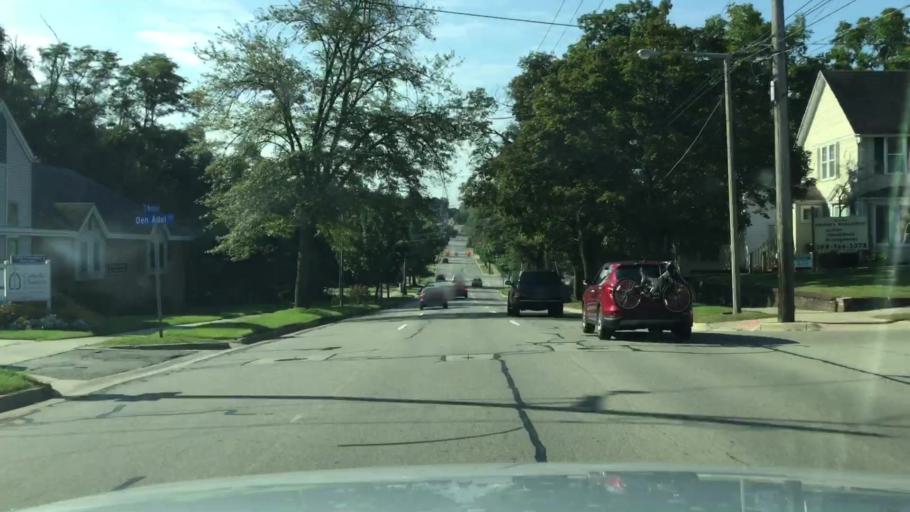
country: US
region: Michigan
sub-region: Kalamazoo County
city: Kalamazoo
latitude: 42.2780
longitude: -85.5896
